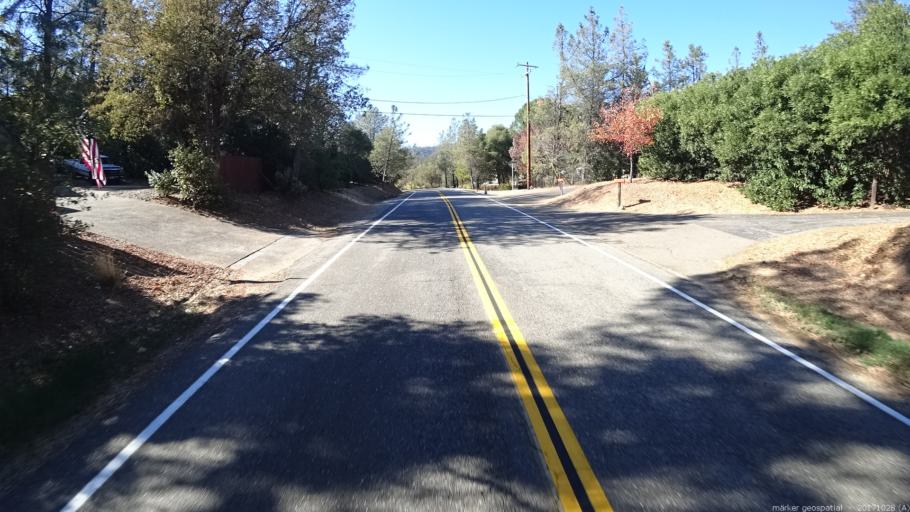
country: US
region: California
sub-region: Shasta County
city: Shasta
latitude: 40.6170
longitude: -122.4861
